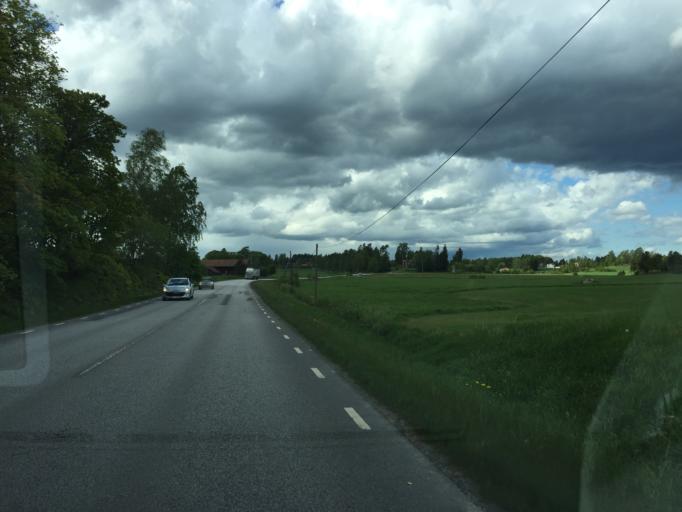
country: SE
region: OEstergoetland
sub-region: Finspangs Kommun
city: Finspang
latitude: 58.6702
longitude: 15.7588
